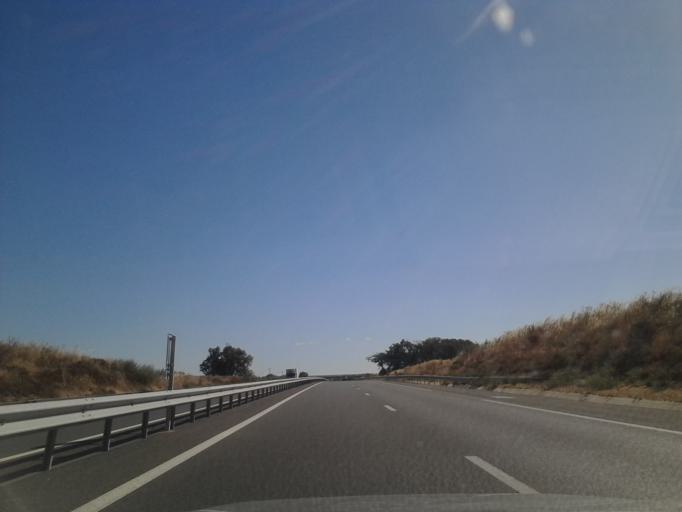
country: FR
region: Languedoc-Roussillon
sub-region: Departement de l'Herault
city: Boujan-sur-Libron
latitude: 43.3751
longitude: 3.2934
